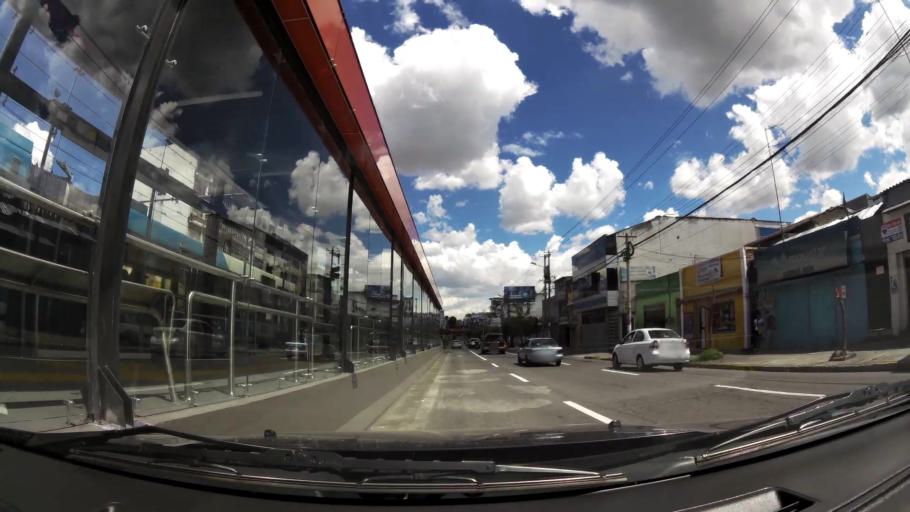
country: EC
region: Pichincha
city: Quito
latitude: -0.1920
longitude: -78.4935
